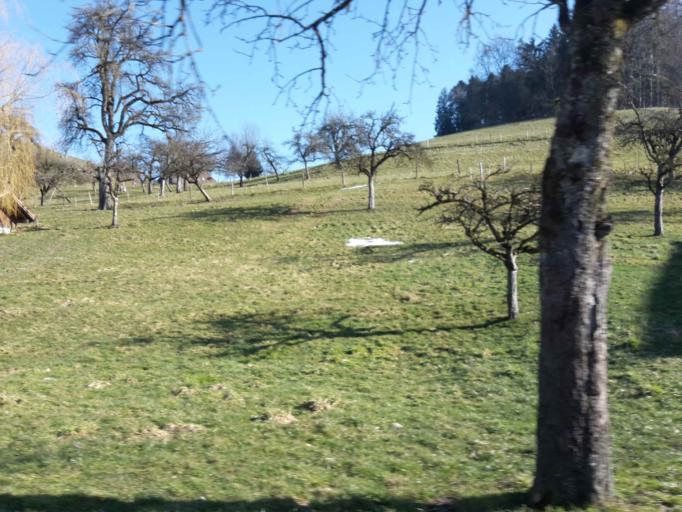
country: CH
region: Bern
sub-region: Emmental District
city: Durrenroth
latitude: 47.1140
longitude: 7.7797
